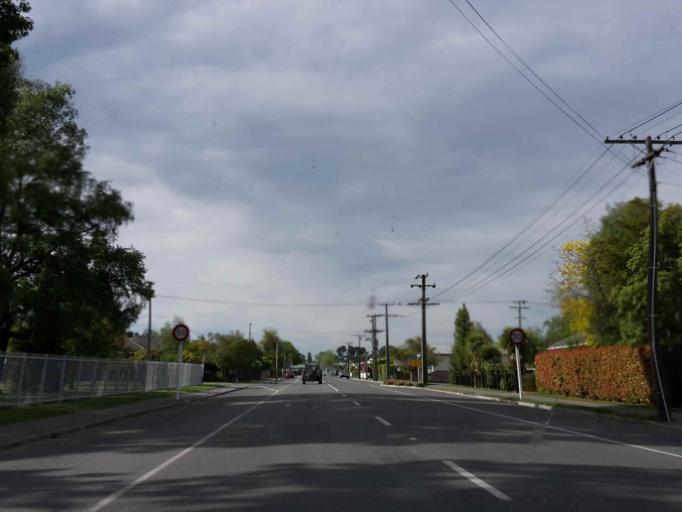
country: NZ
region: Canterbury
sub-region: Timaru District
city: Pleasant Point
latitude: -44.0969
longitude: 171.2398
